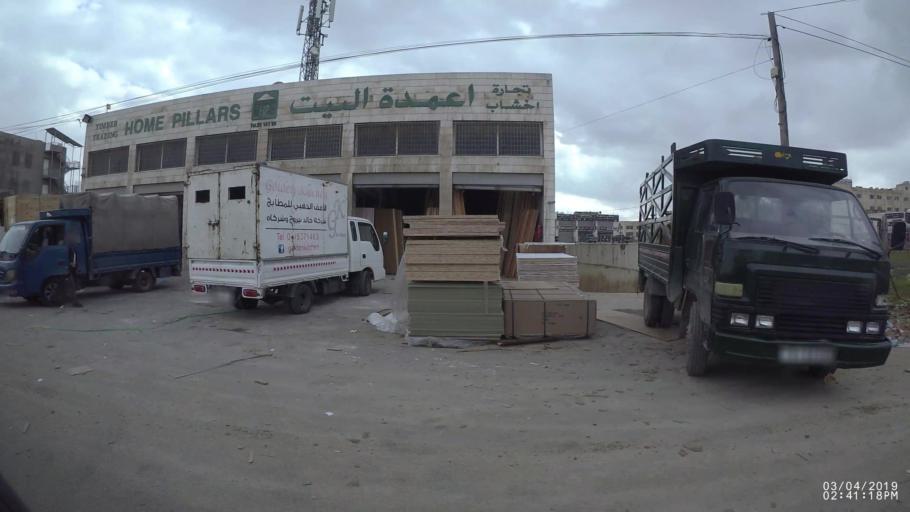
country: JO
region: Amman
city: Wadi as Sir
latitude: 31.9405
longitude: 35.8416
